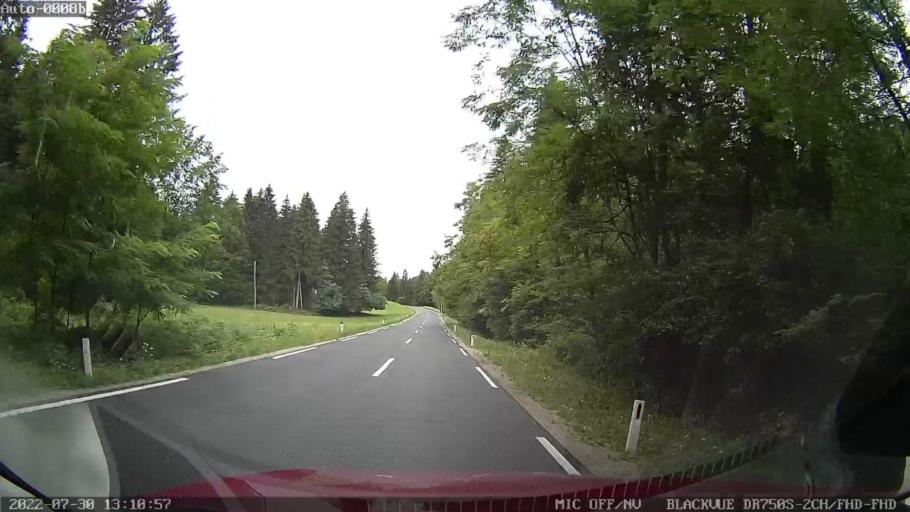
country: SI
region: Dolenjske Toplice
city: Dolenjske Toplice
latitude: 45.6991
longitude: 15.0829
